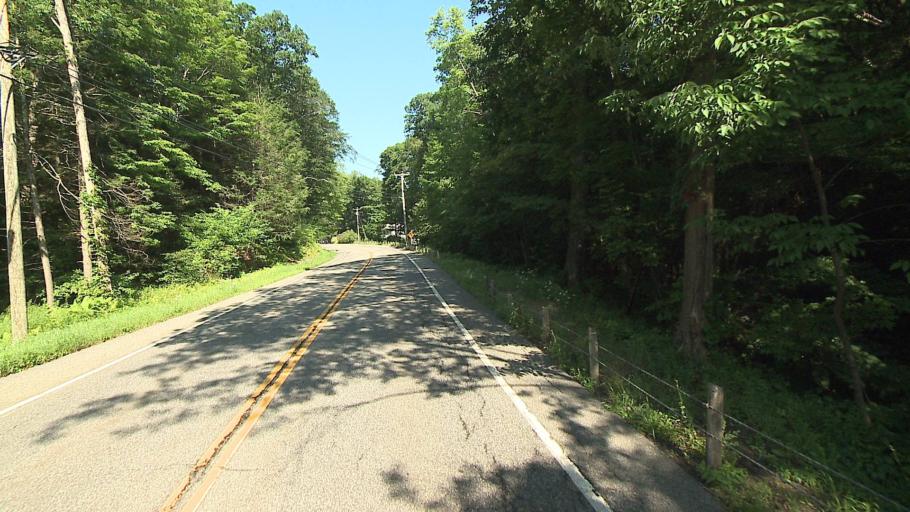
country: US
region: Connecticut
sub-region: Litchfield County
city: Kent
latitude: 41.8245
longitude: -73.4105
